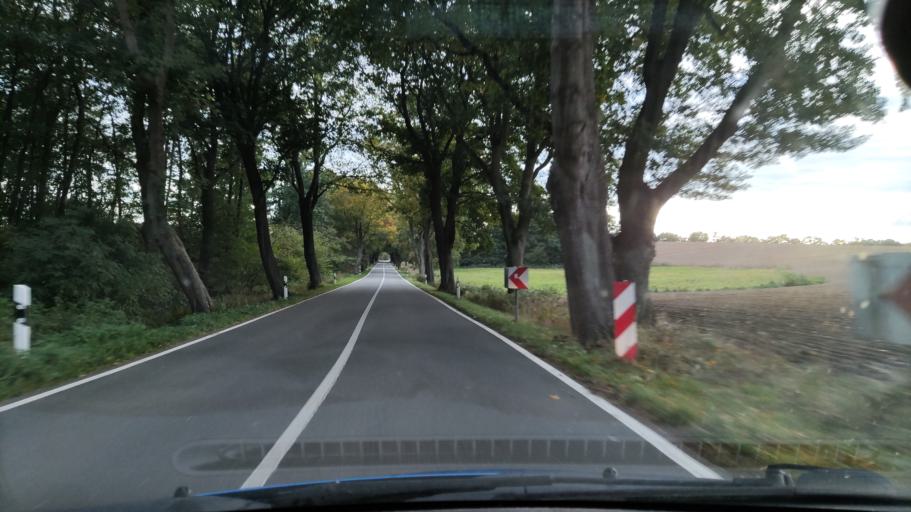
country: DE
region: Mecklenburg-Vorpommern
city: Zarrentin
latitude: 53.4356
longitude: 10.8598
